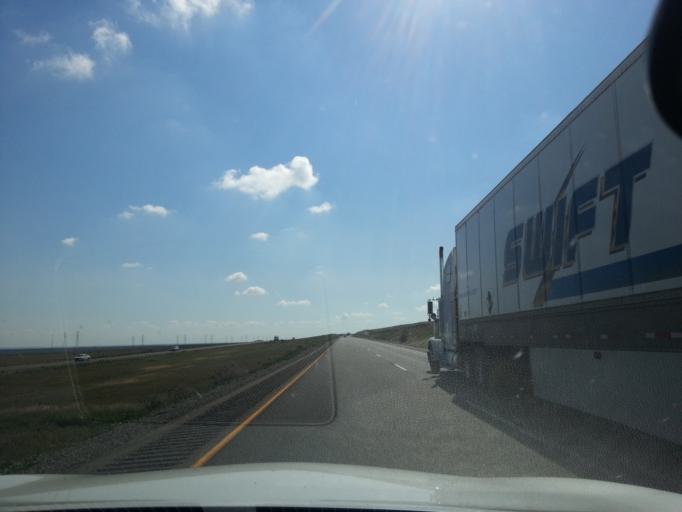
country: US
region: California
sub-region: Fresno County
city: Mendota
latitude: 36.5007
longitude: -120.4546
